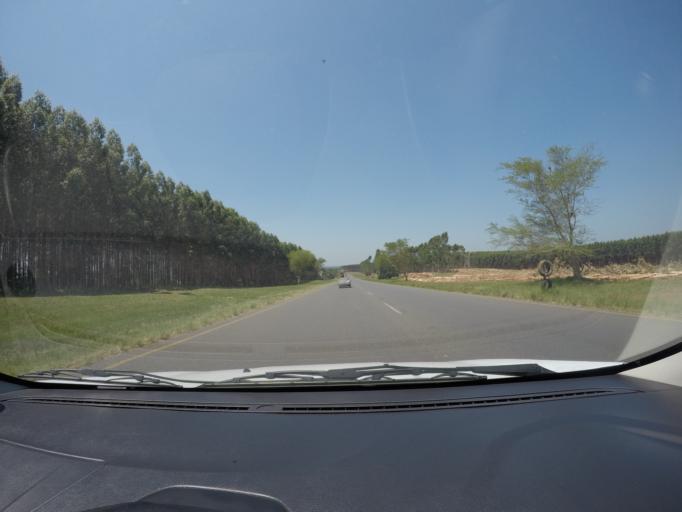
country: ZA
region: KwaZulu-Natal
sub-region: uThungulu District Municipality
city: eSikhawini
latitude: -28.8207
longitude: 31.9497
